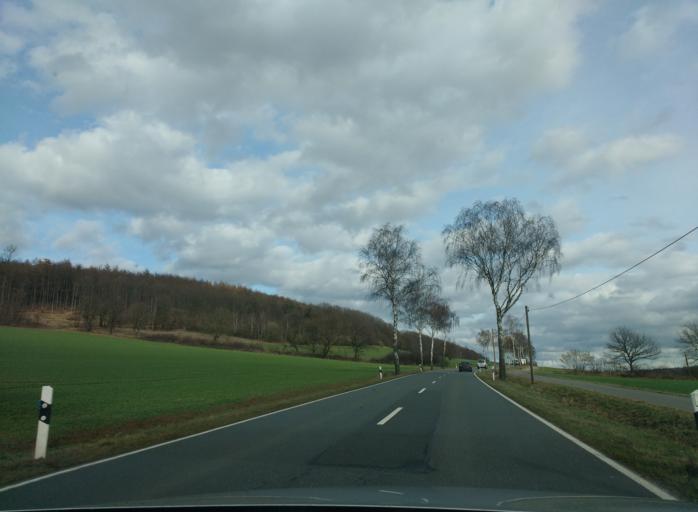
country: DE
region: Lower Saxony
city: Rinteln
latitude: 52.1546
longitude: 8.9820
